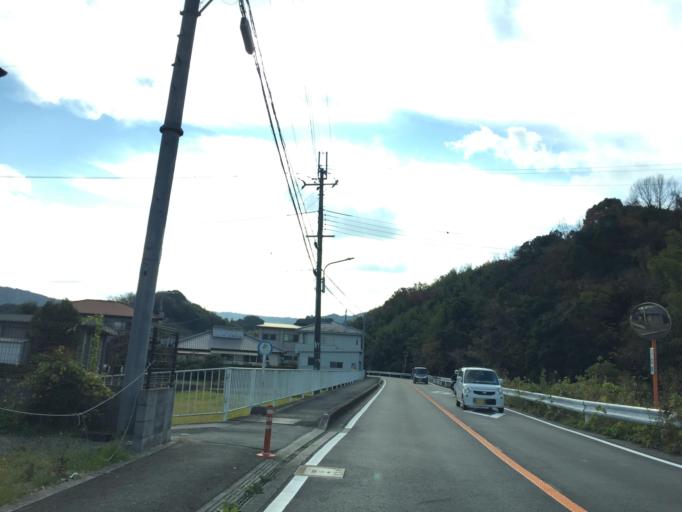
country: JP
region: Wakayama
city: Kainan
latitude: 34.1690
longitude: 135.2507
